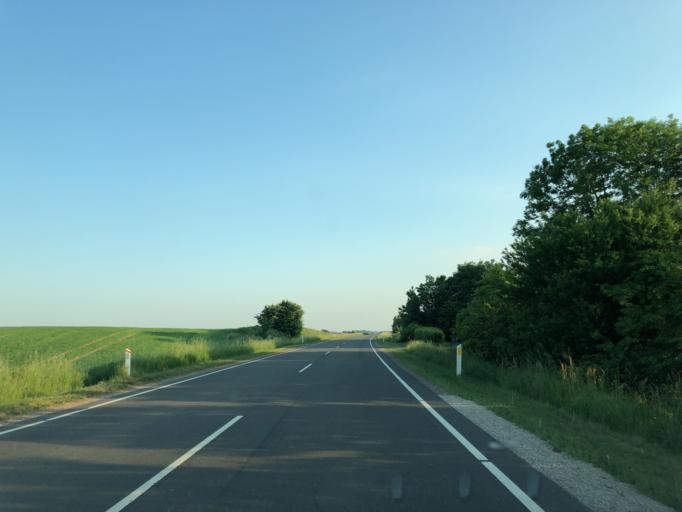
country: DK
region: Central Jutland
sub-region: Struer Kommune
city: Struer
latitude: 56.4636
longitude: 8.5458
